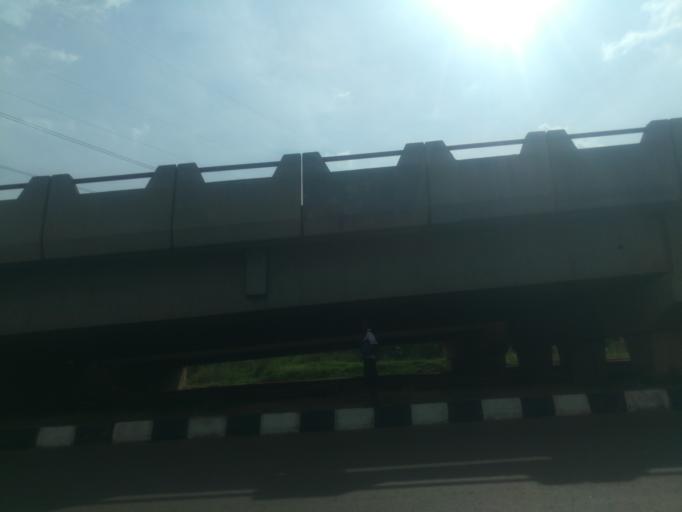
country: NG
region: Ogun
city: Abeokuta
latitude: 7.1253
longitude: 3.3584
